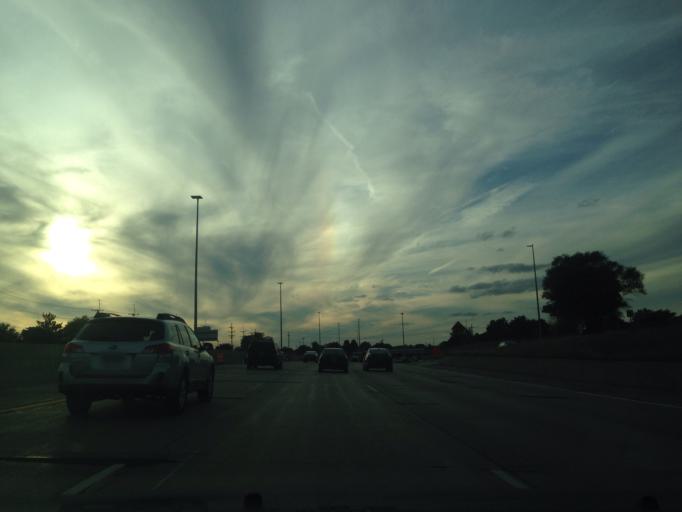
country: US
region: Michigan
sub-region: Wayne County
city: Plymouth
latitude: 42.3817
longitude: -83.4174
